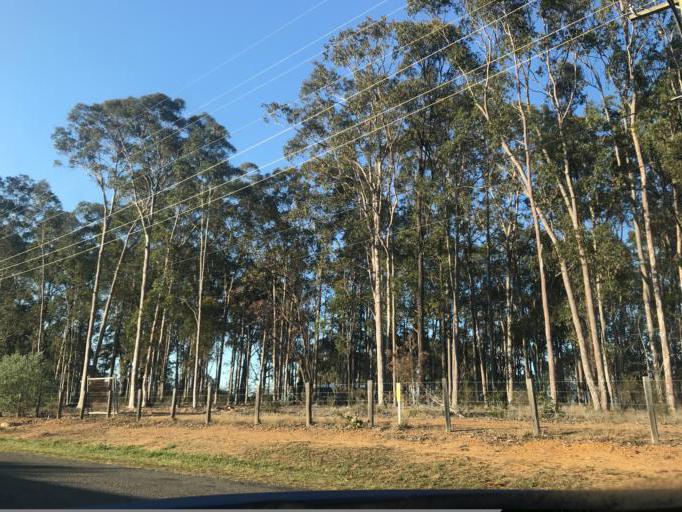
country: AU
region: New South Wales
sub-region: Cessnock
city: Cessnock
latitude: -32.9038
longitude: 151.2820
